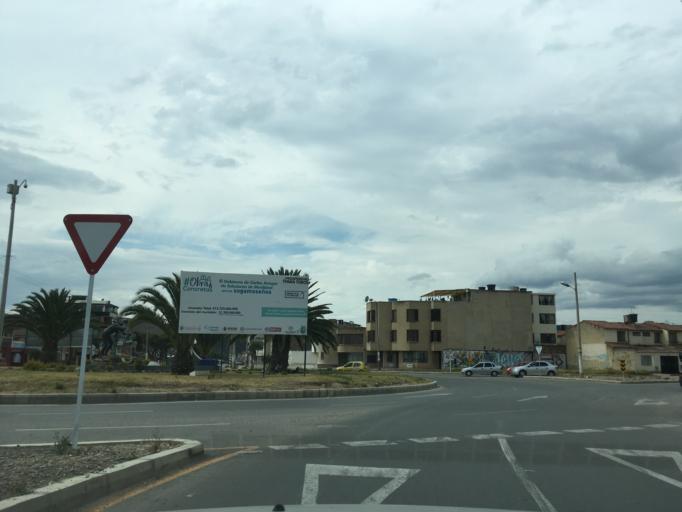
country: CO
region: Boyaca
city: Sogamoso
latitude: 5.7136
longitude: -72.9357
